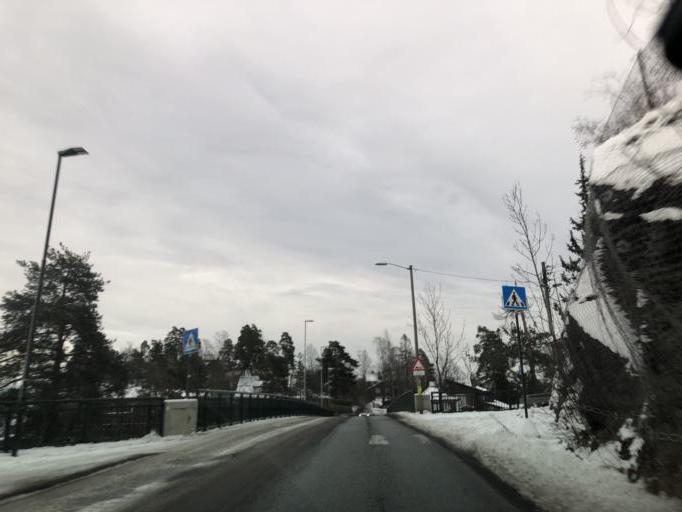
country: NO
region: Akershus
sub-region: Asker
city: Billingstad
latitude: 59.8745
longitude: 10.5057
